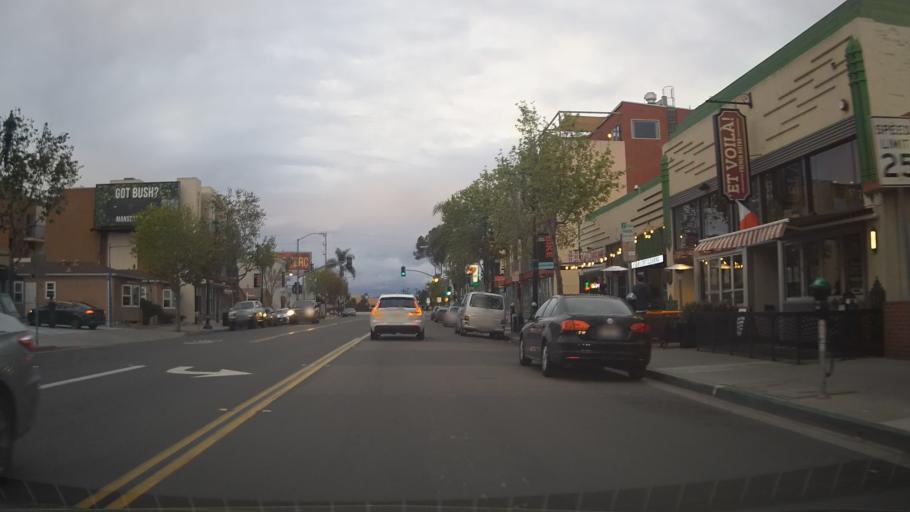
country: US
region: California
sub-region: San Diego County
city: San Diego
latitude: 32.7629
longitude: -117.1302
